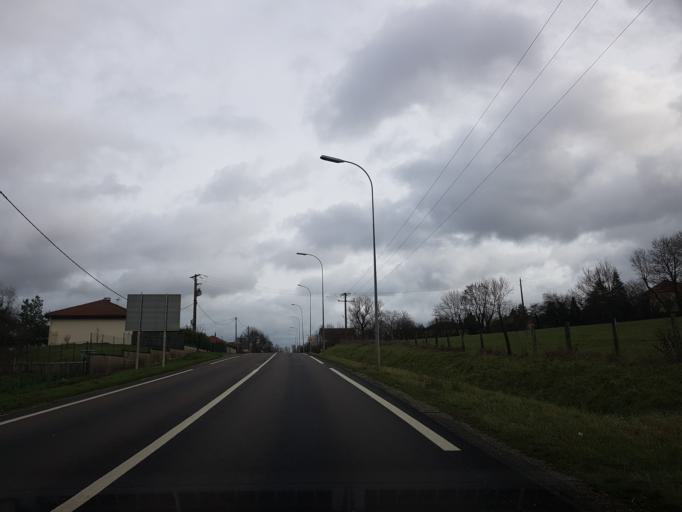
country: FR
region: Champagne-Ardenne
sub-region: Departement de la Haute-Marne
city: Langres
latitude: 47.8722
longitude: 5.3345
